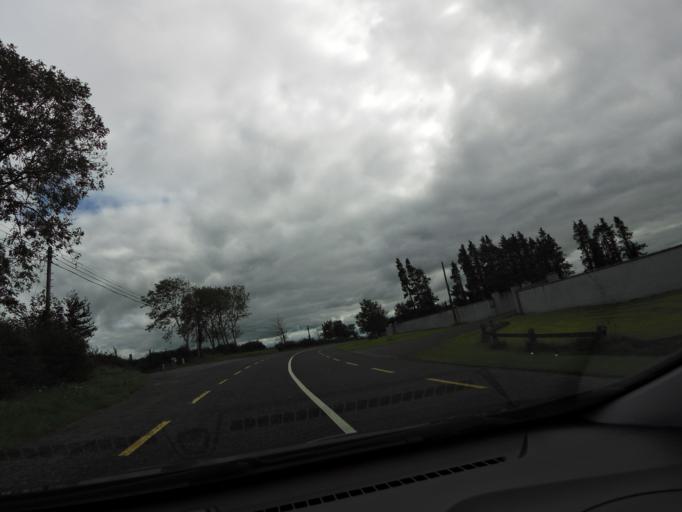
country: IE
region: Connaught
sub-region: County Galway
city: Ballinasloe
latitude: 53.3182
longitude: -8.1731
